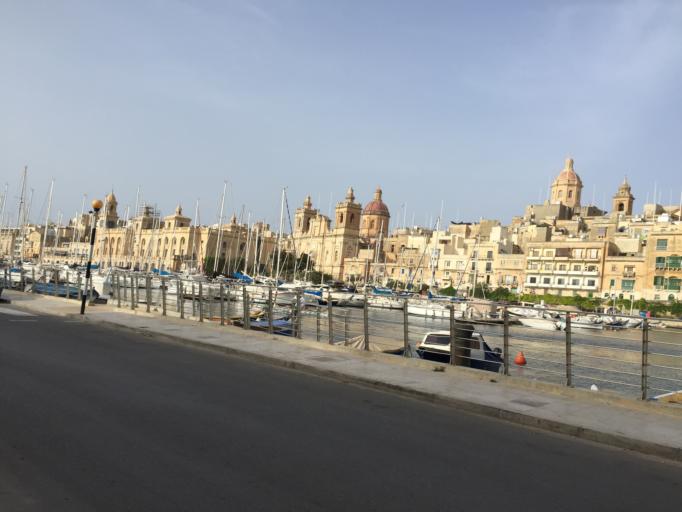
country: MT
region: L-Isla
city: Senglea
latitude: 35.8856
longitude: 14.5200
